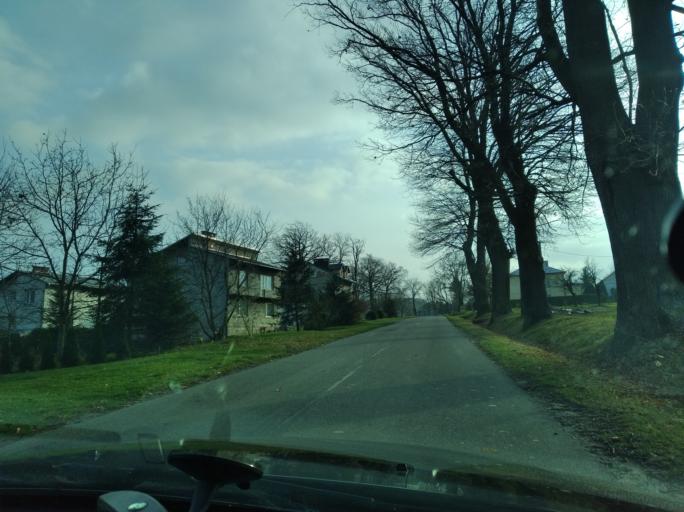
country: PL
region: Subcarpathian Voivodeship
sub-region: Powiat przeworski
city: Lopuszka Wielka
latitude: 49.9523
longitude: 22.4087
